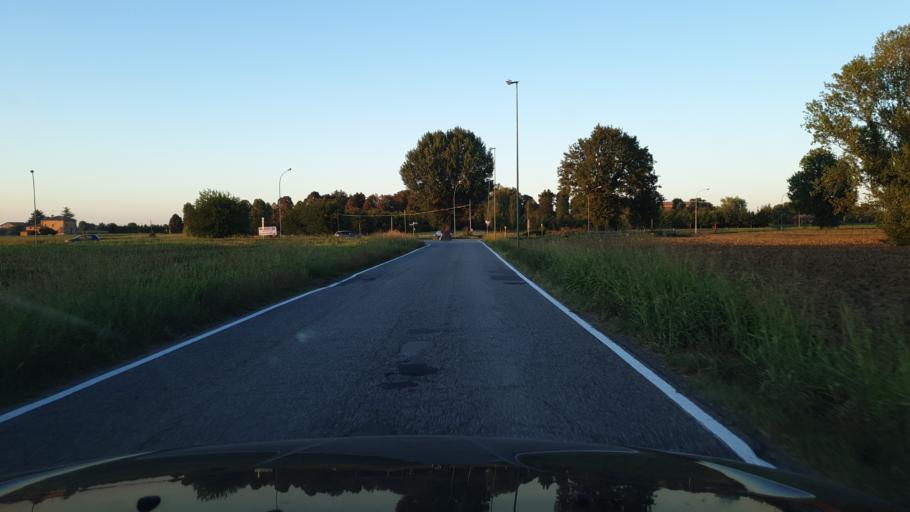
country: IT
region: Emilia-Romagna
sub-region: Provincia di Bologna
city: Quarto Inferiore
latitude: 44.5264
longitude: 11.3933
